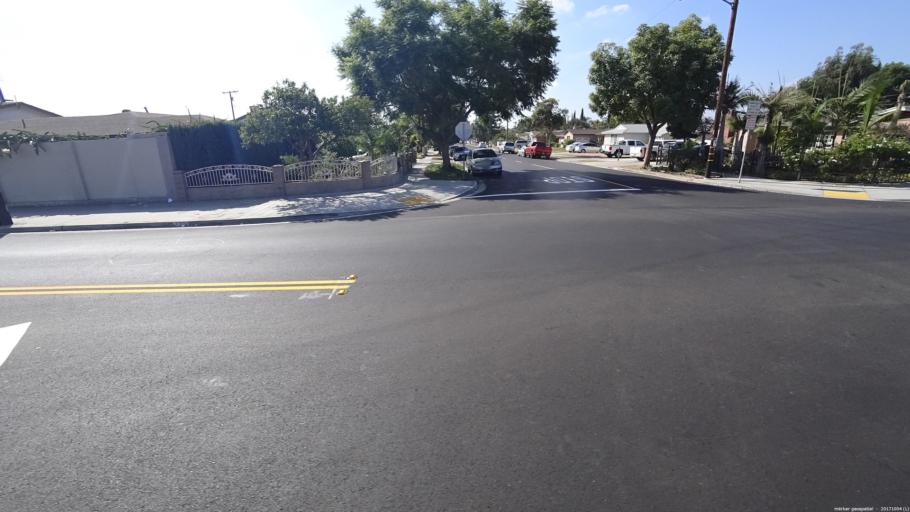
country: US
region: California
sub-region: Orange County
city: Stanton
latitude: 33.7957
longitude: -117.9880
